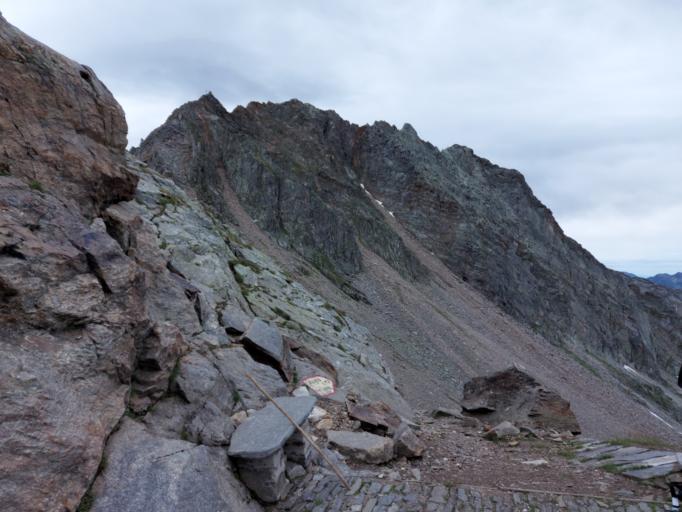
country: IT
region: Piedmont
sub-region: Provincia di Vercelli
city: Rima
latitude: 45.9028
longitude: 7.9580
